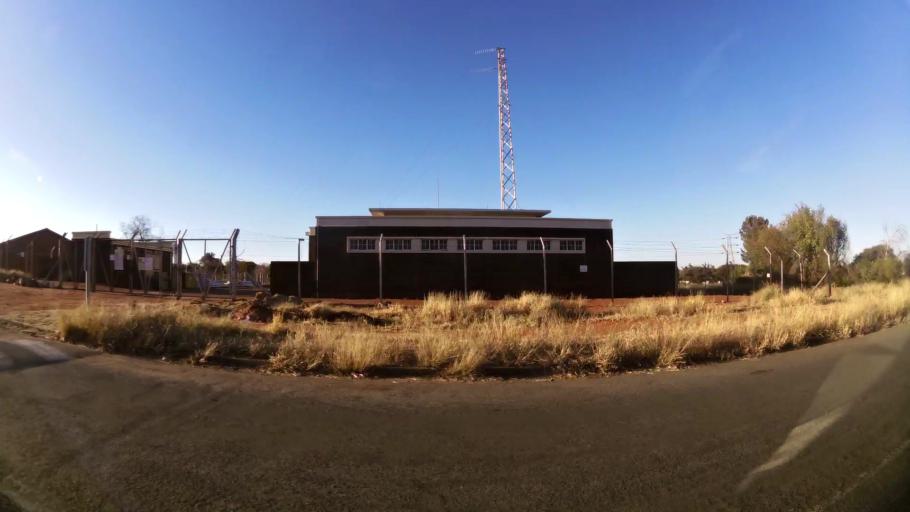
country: ZA
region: Northern Cape
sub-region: Frances Baard District Municipality
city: Kimberley
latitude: -28.7605
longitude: 24.7438
